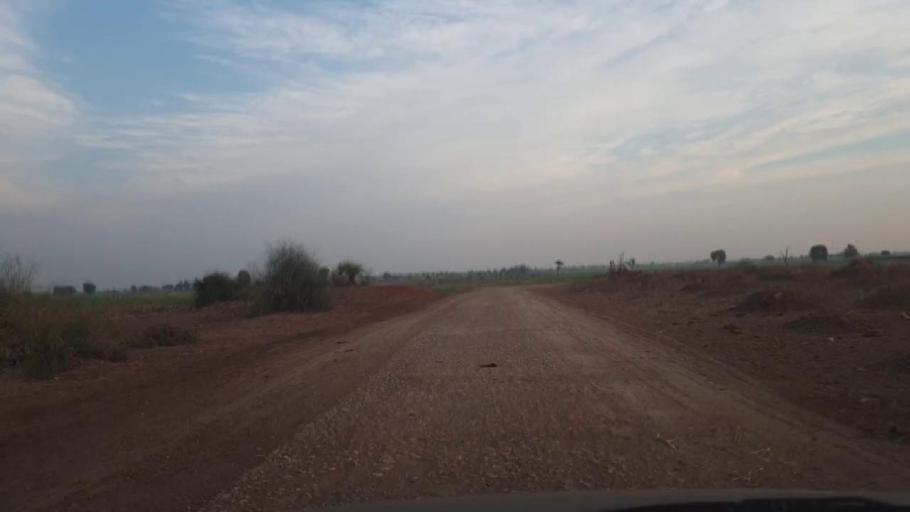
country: PK
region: Sindh
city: Shahpur Chakar
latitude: 26.0594
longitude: 68.5294
